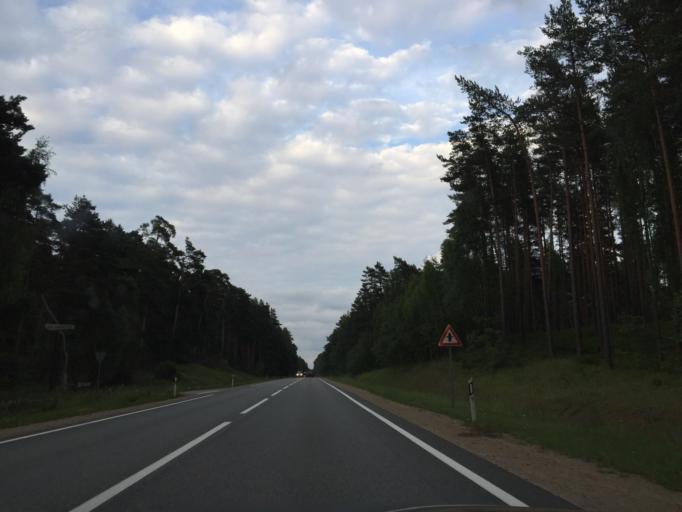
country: LV
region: Babite
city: Pinki
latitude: 56.9226
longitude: 23.8882
